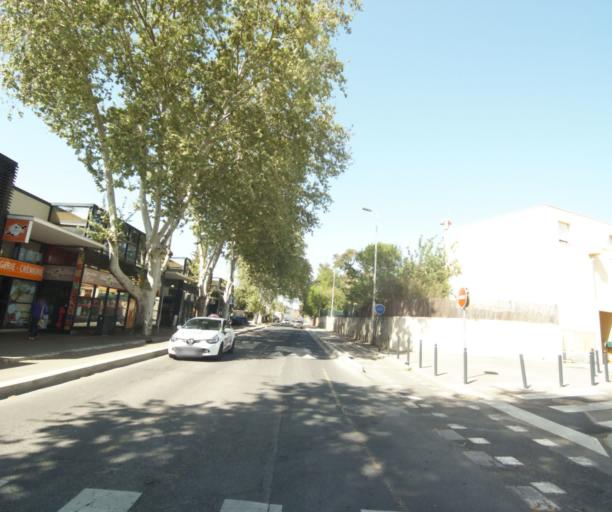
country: FR
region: Languedoc-Roussillon
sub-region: Departement de l'Herault
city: Castelnau-le-Lez
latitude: 43.6206
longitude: 3.8975
